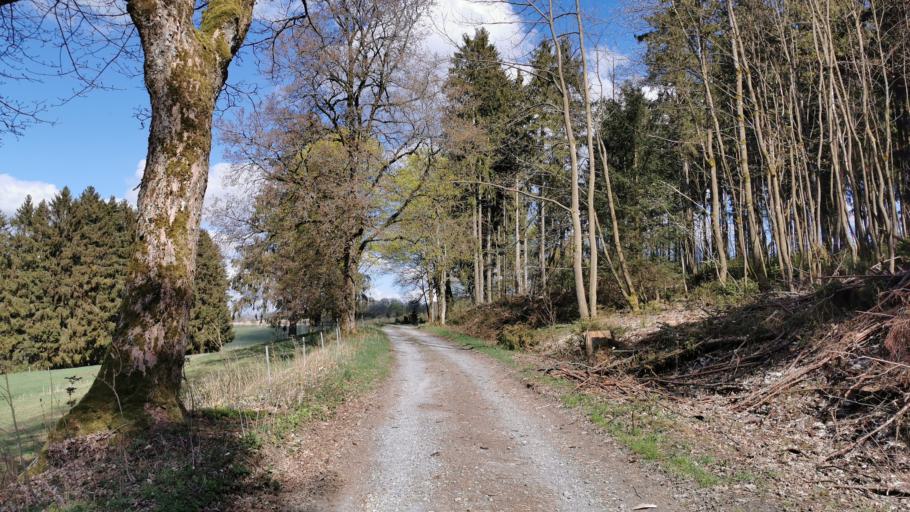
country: DE
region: Bavaria
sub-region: Upper Franconia
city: Ludwigsstadt
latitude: 50.4679
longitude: 11.4219
